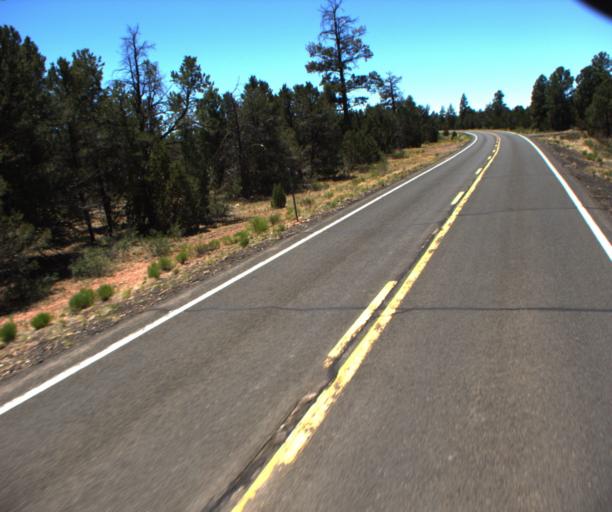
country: US
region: Arizona
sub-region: Gila County
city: Star Valley
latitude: 34.6921
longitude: -111.1096
